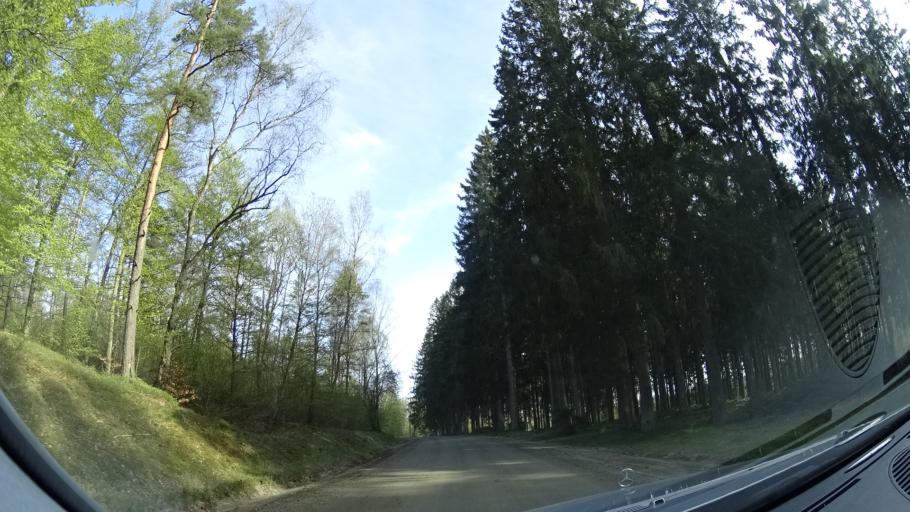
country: SE
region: Skane
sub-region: Hassleholms Kommun
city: Sosdala
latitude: 56.0913
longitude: 13.6696
